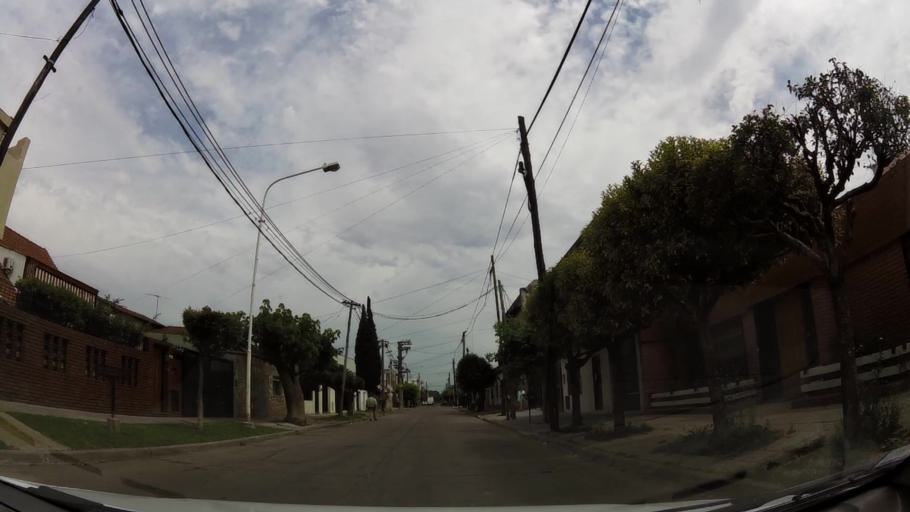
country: AR
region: Buenos Aires F.D.
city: Villa Lugano
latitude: -34.6865
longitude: -58.5022
